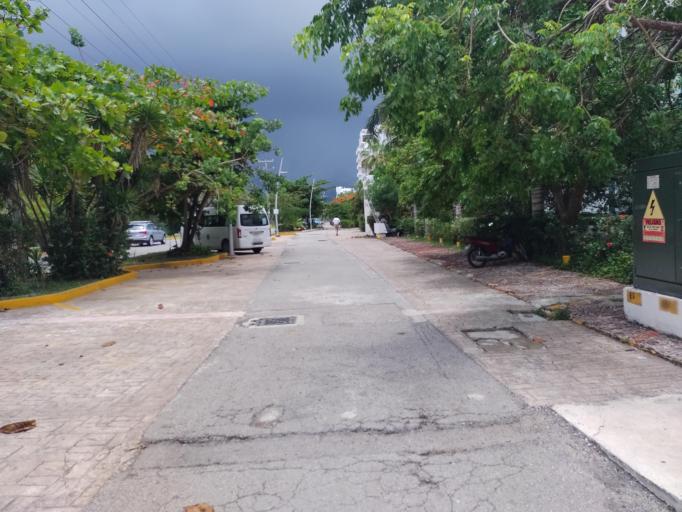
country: MX
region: Quintana Roo
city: San Miguel de Cozumel
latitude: 20.5347
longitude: -86.9381
